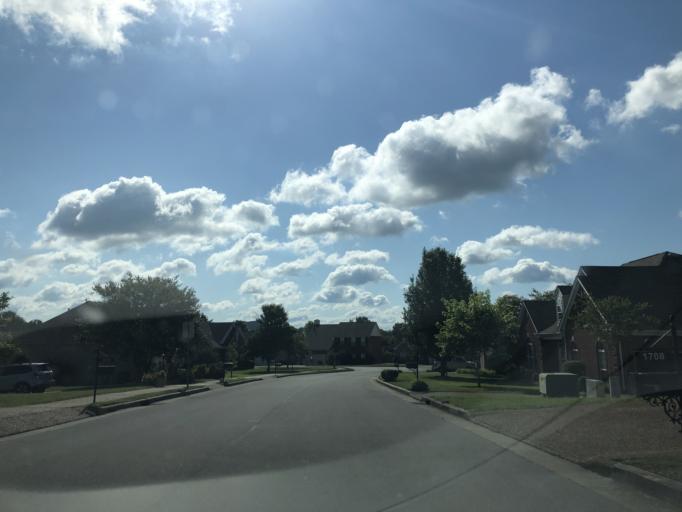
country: US
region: Tennessee
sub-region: Davidson County
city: Belle Meade
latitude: 36.0585
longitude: -86.9503
